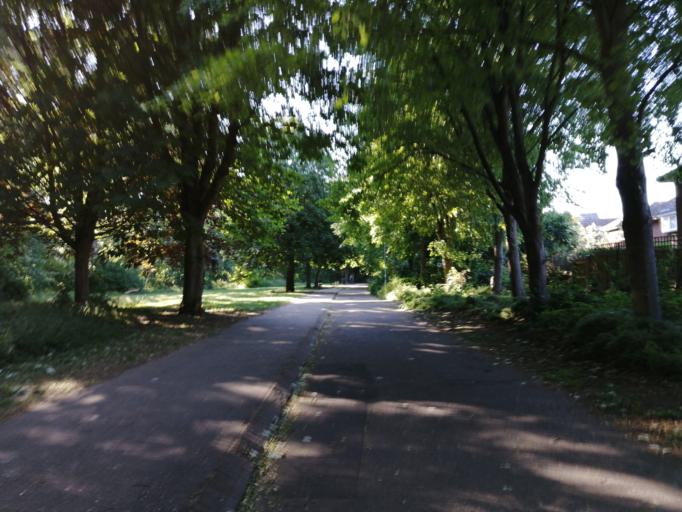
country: GB
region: England
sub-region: Peterborough
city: Marholm
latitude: 52.5977
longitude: -0.2779
